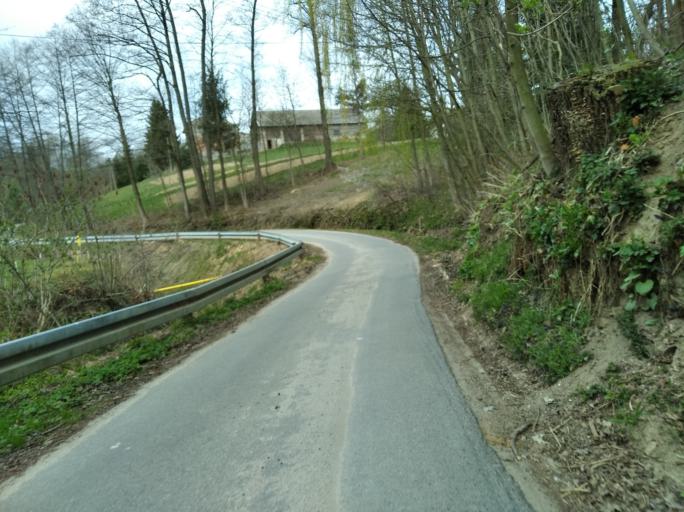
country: PL
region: Subcarpathian Voivodeship
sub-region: Powiat ropczycko-sedziszowski
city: Wielopole Skrzynskie
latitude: 49.9077
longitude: 21.6197
